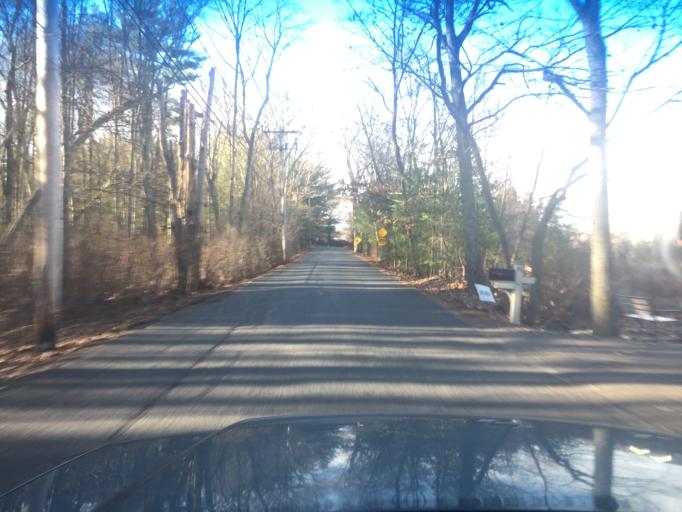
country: US
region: Massachusetts
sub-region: Middlesex County
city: Ashland
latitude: 42.2299
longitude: -71.4835
